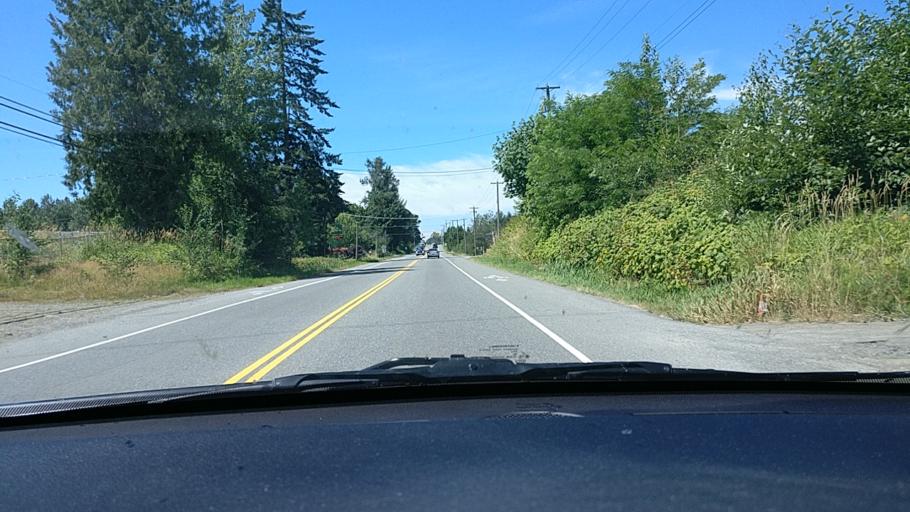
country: CA
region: British Columbia
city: Aldergrove
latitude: 49.0572
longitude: -122.4198
